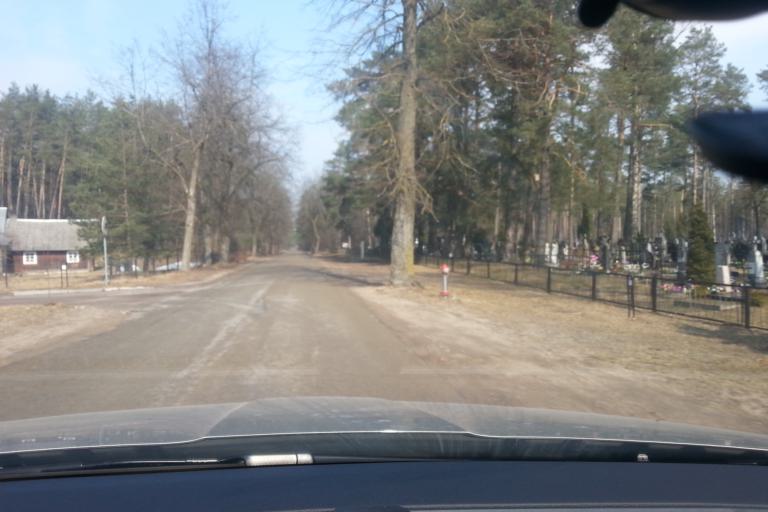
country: LT
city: Trakai
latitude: 54.5047
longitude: 24.9845
